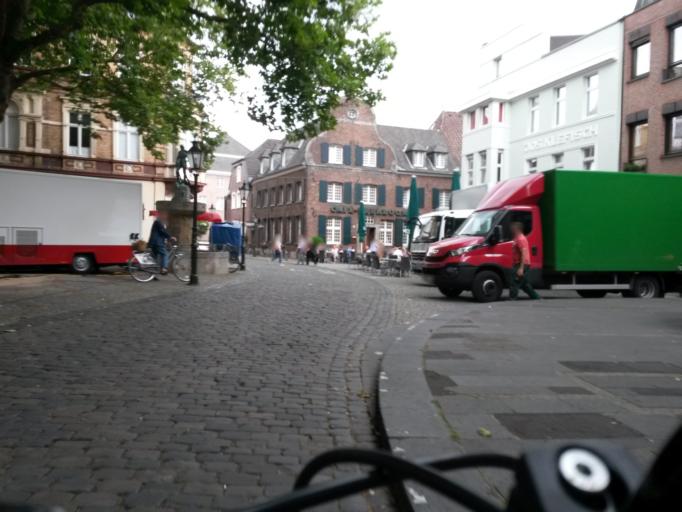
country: DE
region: North Rhine-Westphalia
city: Kempen
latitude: 51.3645
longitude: 6.4185
